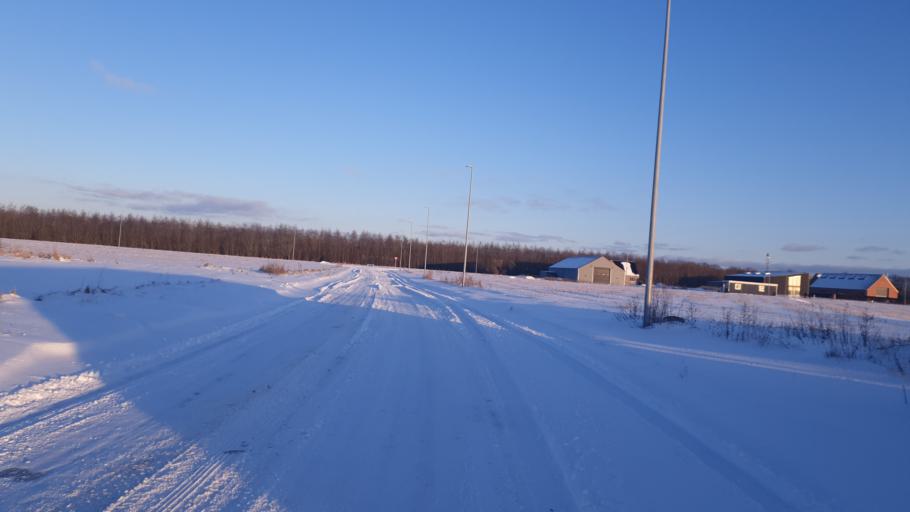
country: DK
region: Central Jutland
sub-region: Hedensted Kommune
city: Hedensted
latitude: 55.7851
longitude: 9.6874
